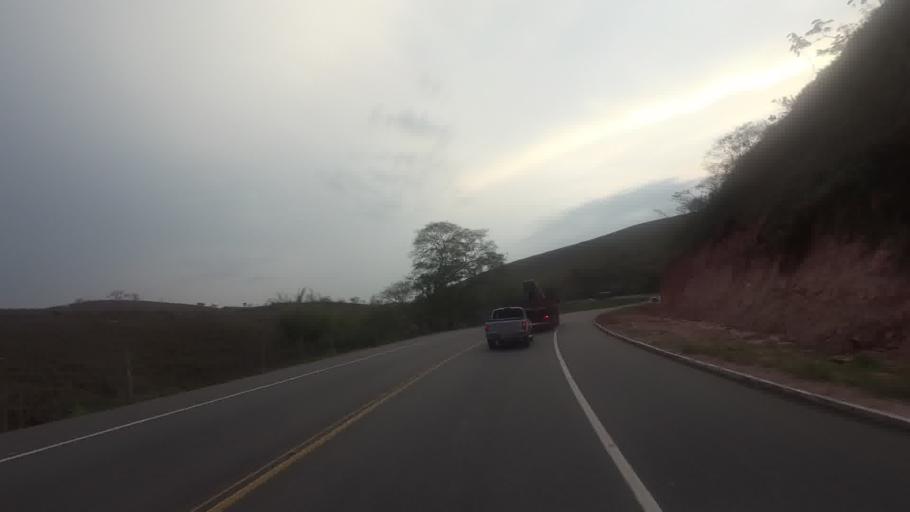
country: BR
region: Rio de Janeiro
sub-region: Carmo
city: Carmo
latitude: -21.8130
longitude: -42.5945
